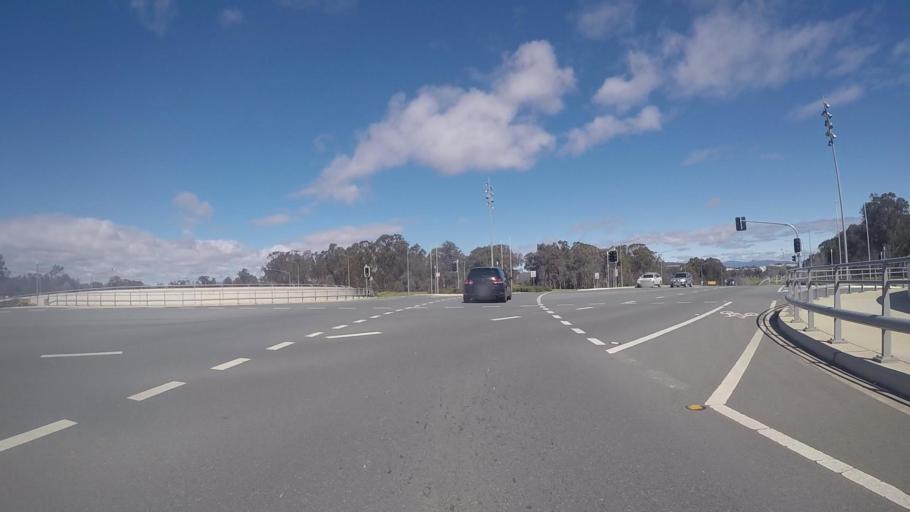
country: AU
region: Australian Capital Territory
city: Canberra
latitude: -35.2988
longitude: 149.1481
